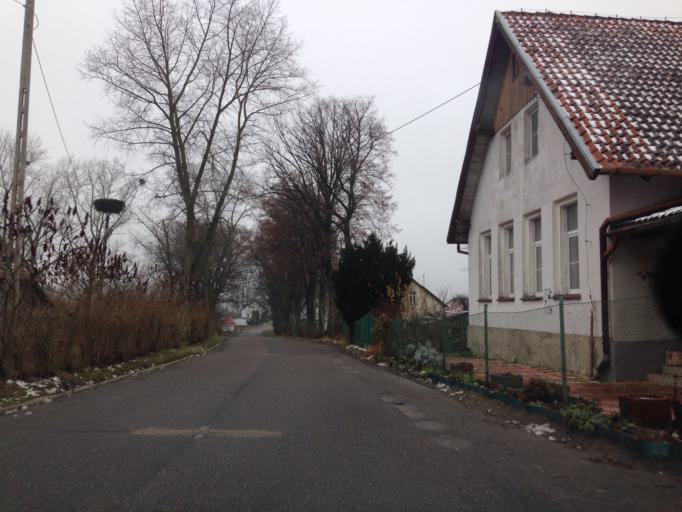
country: PL
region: Warmian-Masurian Voivodeship
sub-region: Powiat gizycki
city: Ryn
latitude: 53.9960
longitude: 21.5101
